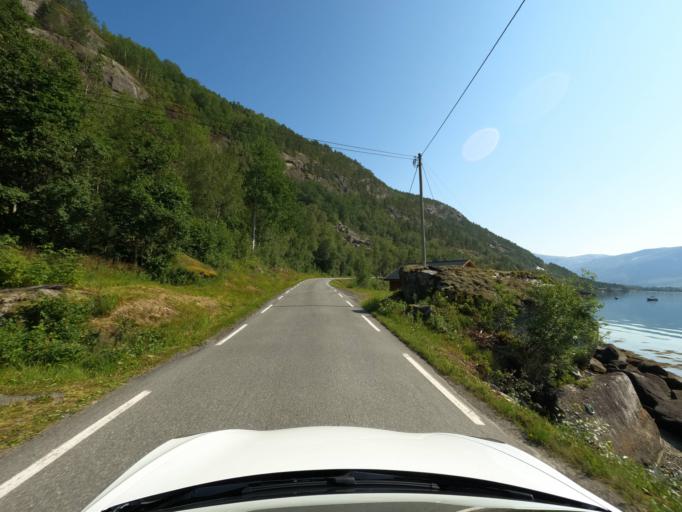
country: NO
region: Nordland
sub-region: Narvik
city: Narvik
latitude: 68.2748
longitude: 17.3967
